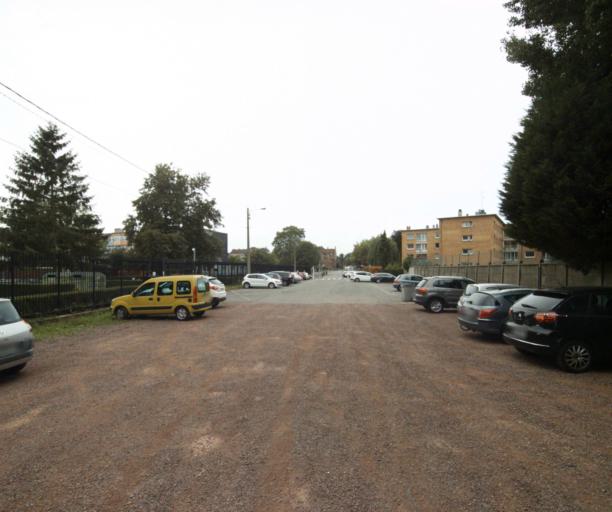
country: FR
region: Nord-Pas-de-Calais
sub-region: Departement du Nord
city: Lambersart
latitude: 50.6476
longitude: 3.0399
